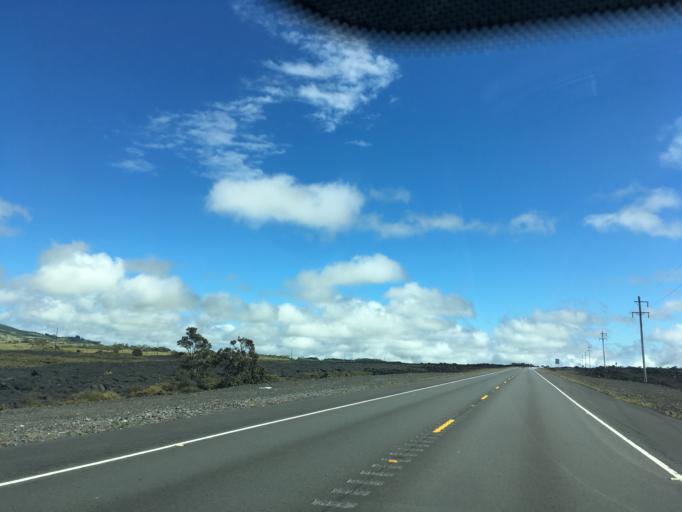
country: US
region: Hawaii
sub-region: Hawaii County
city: Volcano
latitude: 19.6845
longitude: -155.4302
